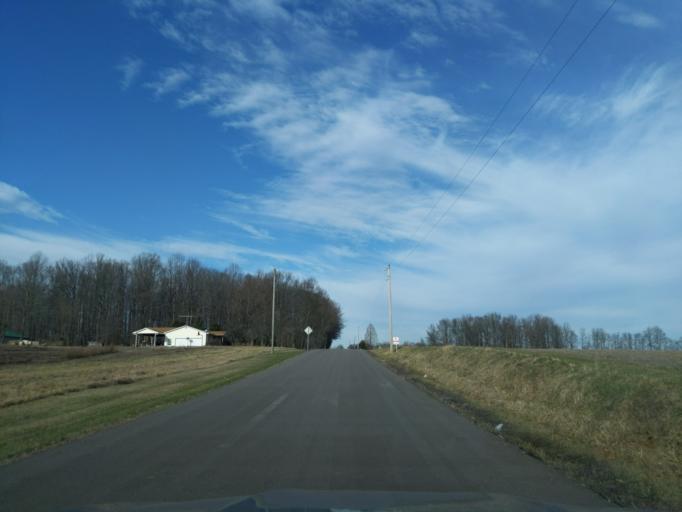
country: US
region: Indiana
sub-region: Decatur County
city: Greensburg
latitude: 39.2273
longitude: -85.4296
